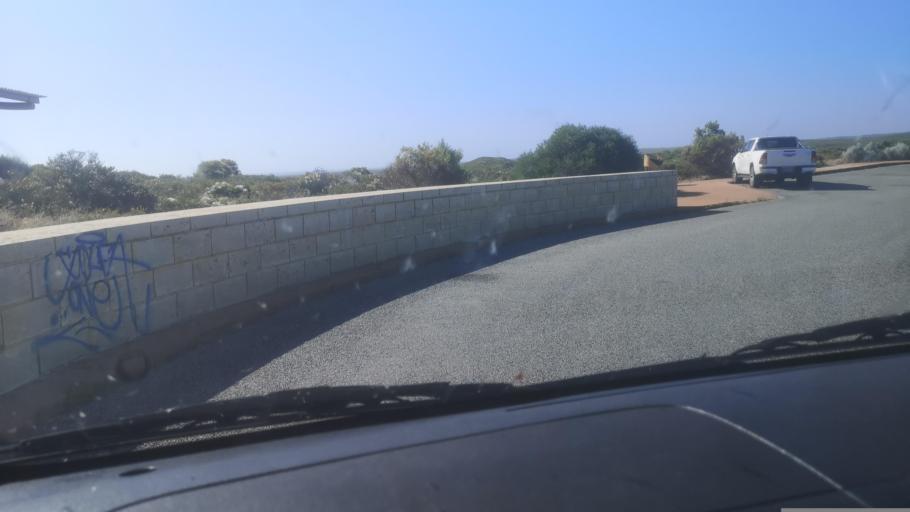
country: AU
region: Western Australia
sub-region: Dandaragan
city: Jurien Bay
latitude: -30.7916
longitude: 115.2255
